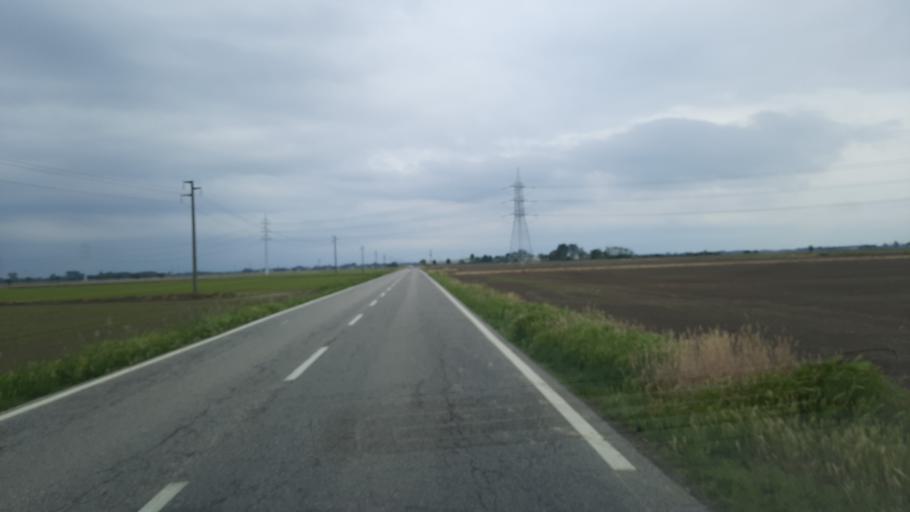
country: IT
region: Lombardy
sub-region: Provincia di Pavia
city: Castelnovetto
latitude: 45.2680
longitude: 8.6181
